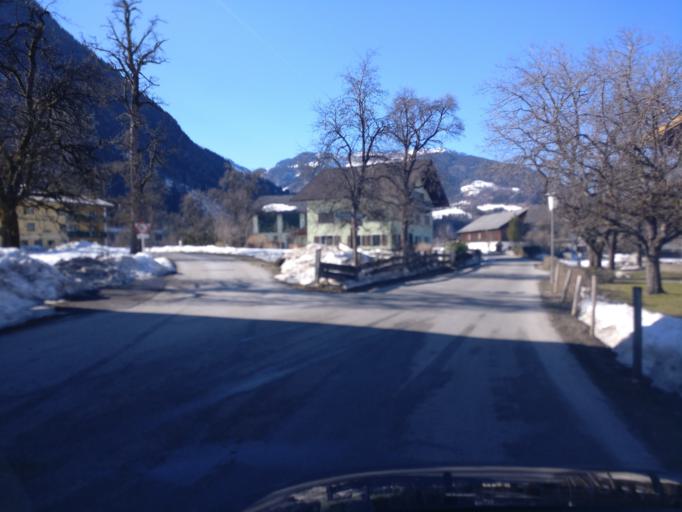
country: AT
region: Salzburg
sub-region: Politischer Bezirk Hallein
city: Golling an der Salzach
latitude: 47.5969
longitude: 13.1562
